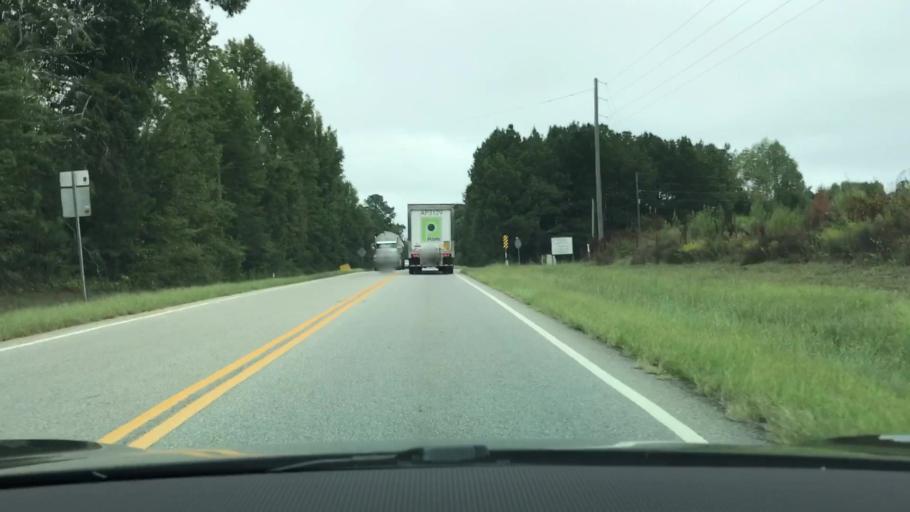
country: US
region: Georgia
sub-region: Greene County
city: Greensboro
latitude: 33.6174
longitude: -83.2107
